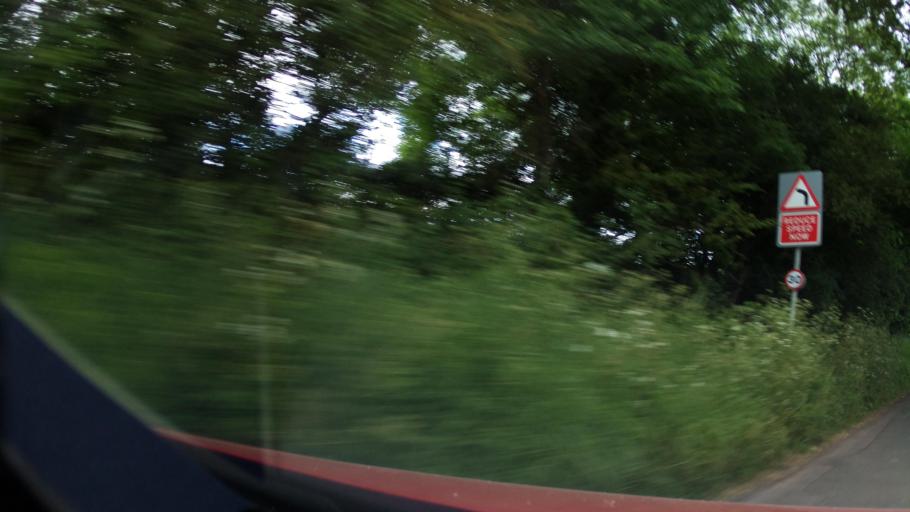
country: GB
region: England
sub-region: South Gloucestershire
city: Siston
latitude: 51.4593
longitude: -2.4452
